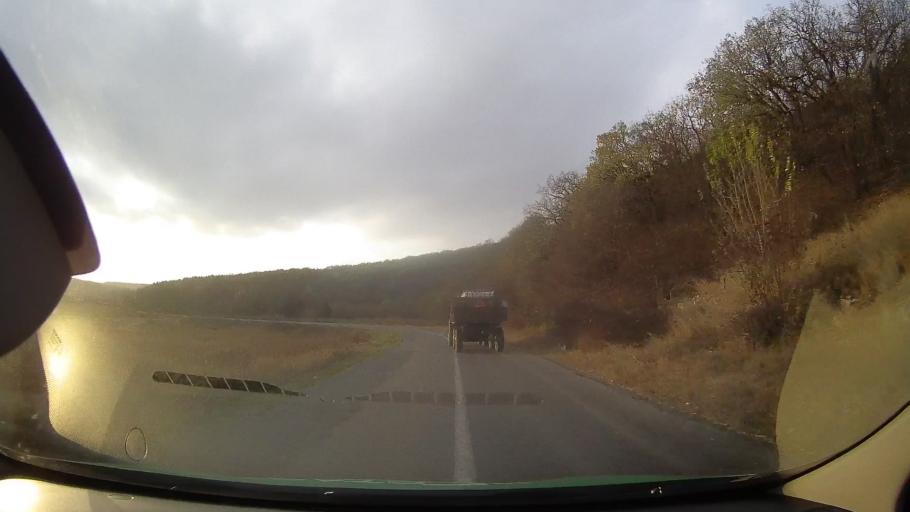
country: RO
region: Constanta
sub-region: Comuna Adamclisi
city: Adamclisi
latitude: 44.0400
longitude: 27.9449
